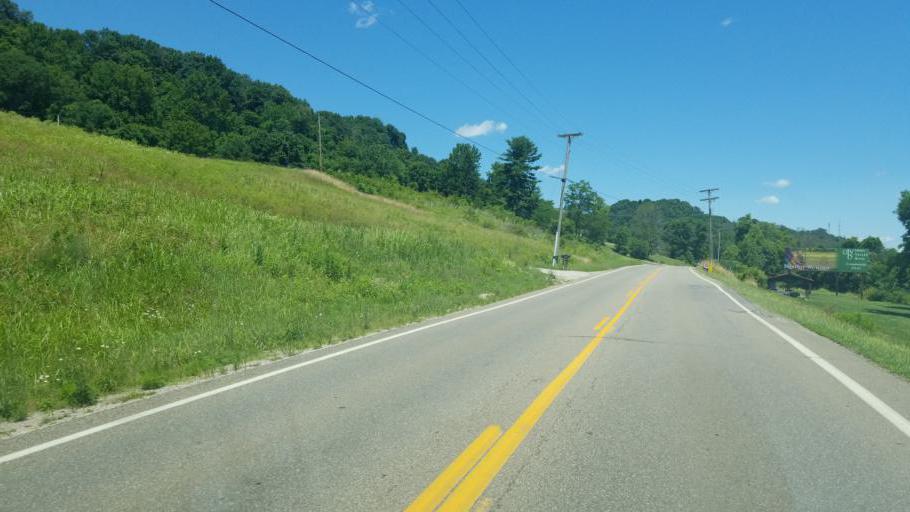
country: US
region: Ohio
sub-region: Gallia County
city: Gallipolis
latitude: 38.7824
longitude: -82.2228
